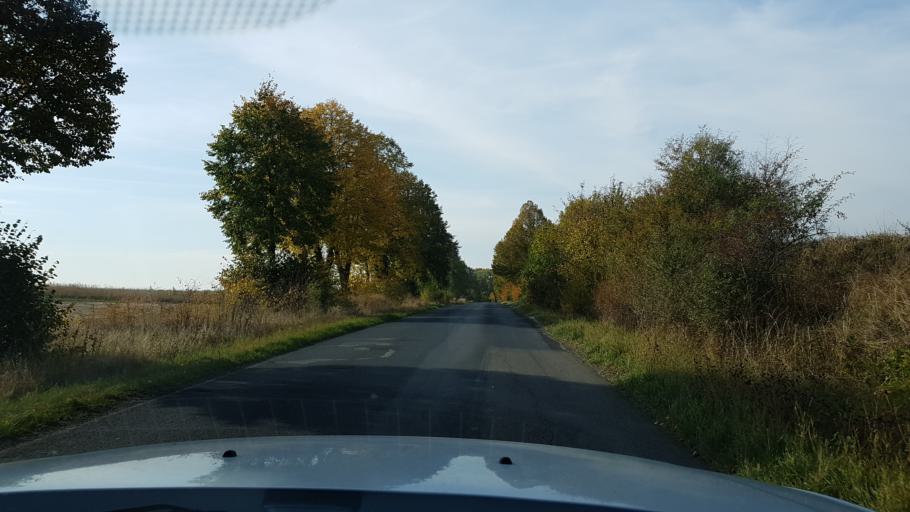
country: PL
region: West Pomeranian Voivodeship
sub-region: Powiat mysliborski
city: Barlinek
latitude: 52.9770
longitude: 15.1716
